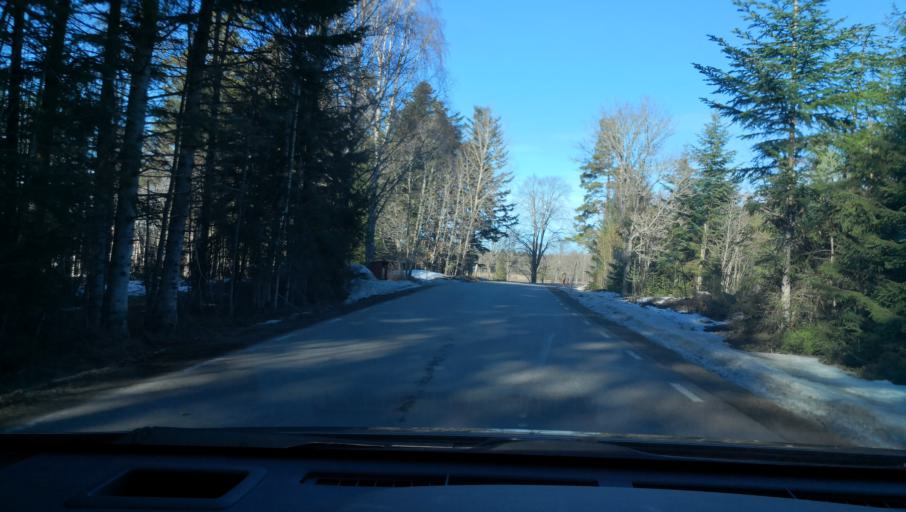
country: SE
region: Uppsala
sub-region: Osthammars Kommun
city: Osterbybruk
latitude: 60.2531
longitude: 17.9455
